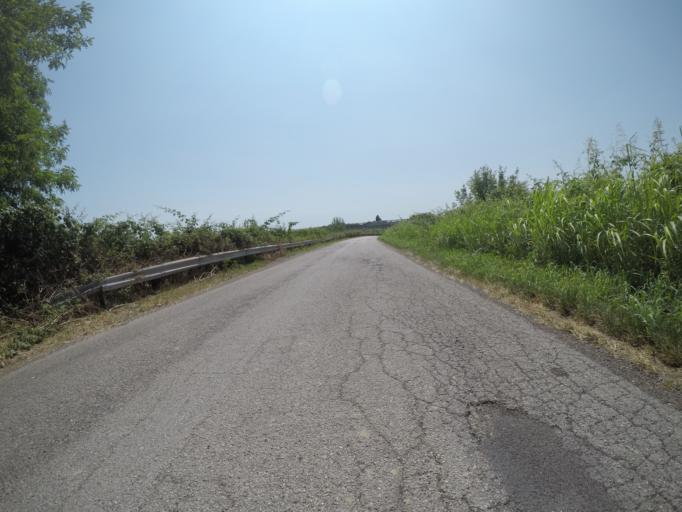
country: IT
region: Veneto
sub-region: Provincia di Rovigo
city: Villamarzana
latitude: 45.0062
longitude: 11.6778
